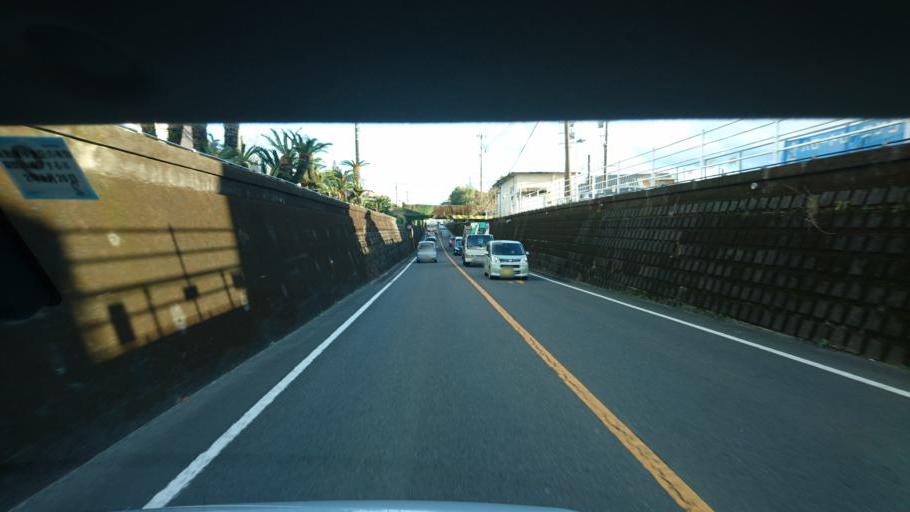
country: JP
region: Miyazaki
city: Miyazaki-shi
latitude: 31.8928
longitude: 131.4196
